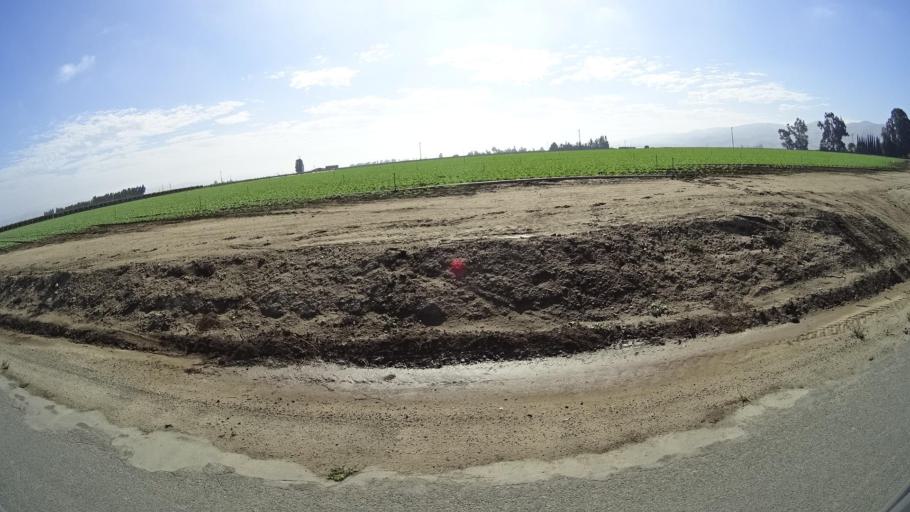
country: US
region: California
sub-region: Monterey County
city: Greenfield
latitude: 36.3237
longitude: -121.2839
